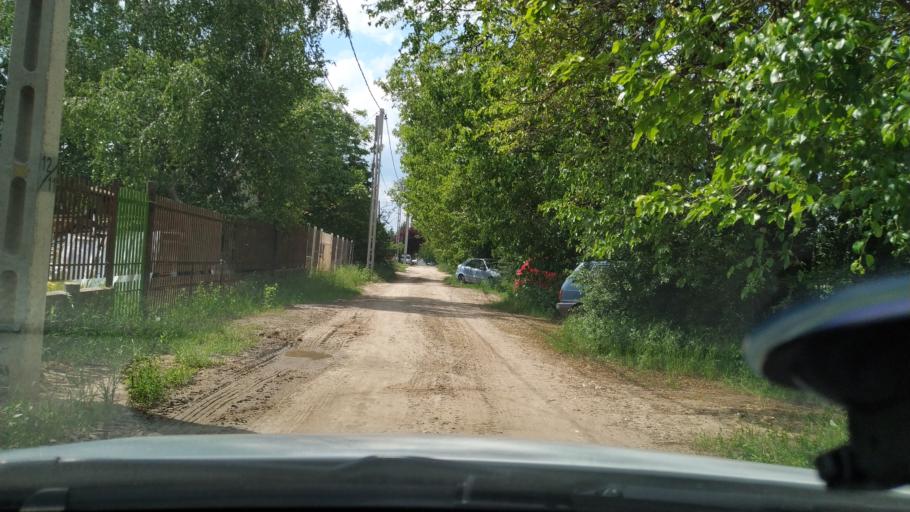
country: HU
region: Pest
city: Peteri
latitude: 47.4092
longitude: 19.4115
